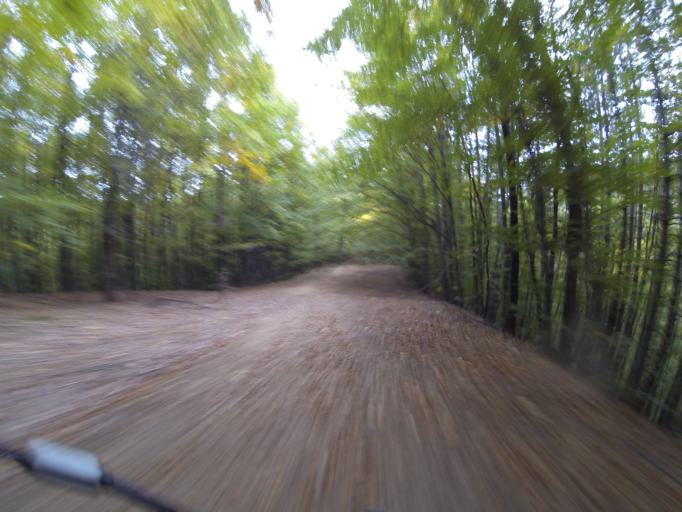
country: RO
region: Gorj
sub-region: Comuna Tismana
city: Sohodol
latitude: 45.0853
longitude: 22.8845
